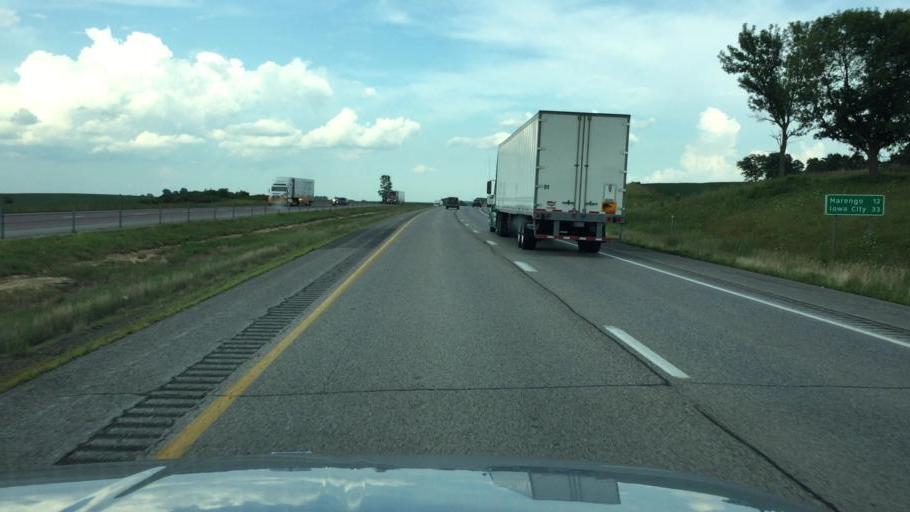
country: US
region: Iowa
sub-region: Iowa County
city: Marengo
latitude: 41.6958
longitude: -92.1472
